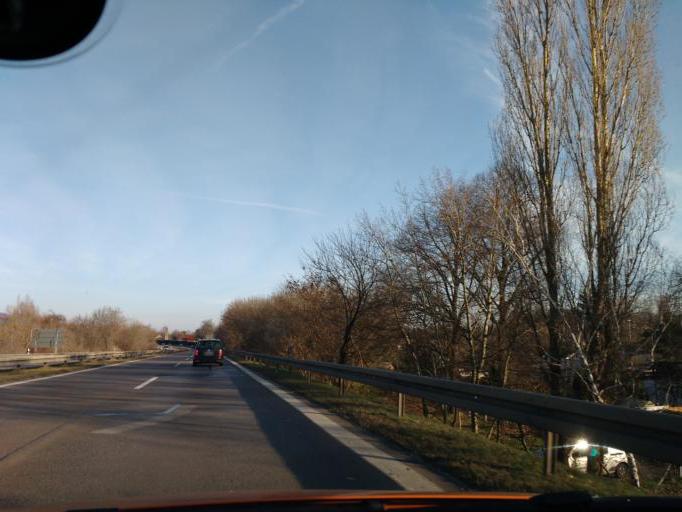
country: DE
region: Berlin
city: Blankenburg
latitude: 52.5922
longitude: 13.4410
